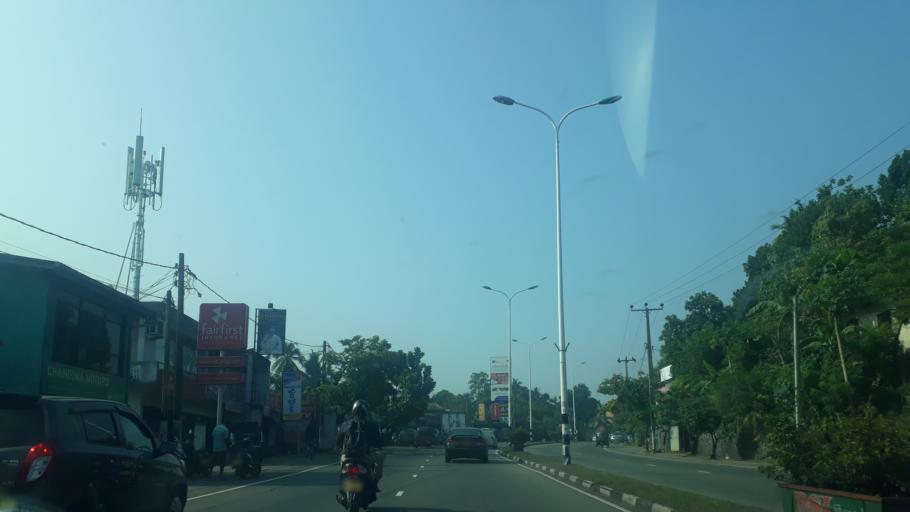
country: LK
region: Western
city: Kelaniya
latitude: 6.9975
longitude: 79.9481
